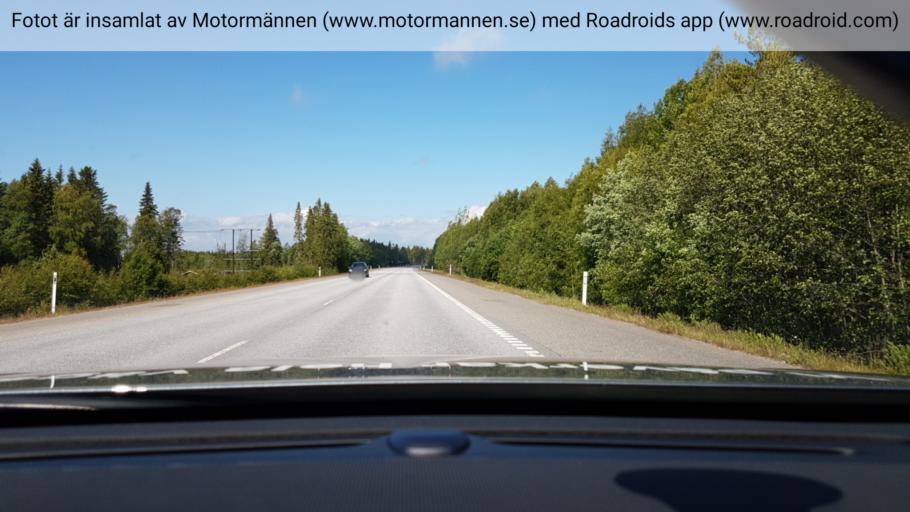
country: SE
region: Vaesterbotten
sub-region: Umea Kommun
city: Holmsund
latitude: 63.7520
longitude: 20.3663
